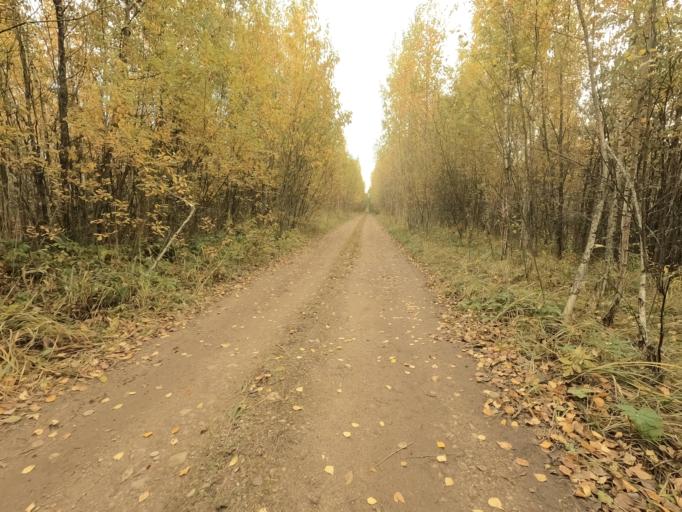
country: RU
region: Novgorod
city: Pankovka
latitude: 58.8760
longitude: 30.8723
